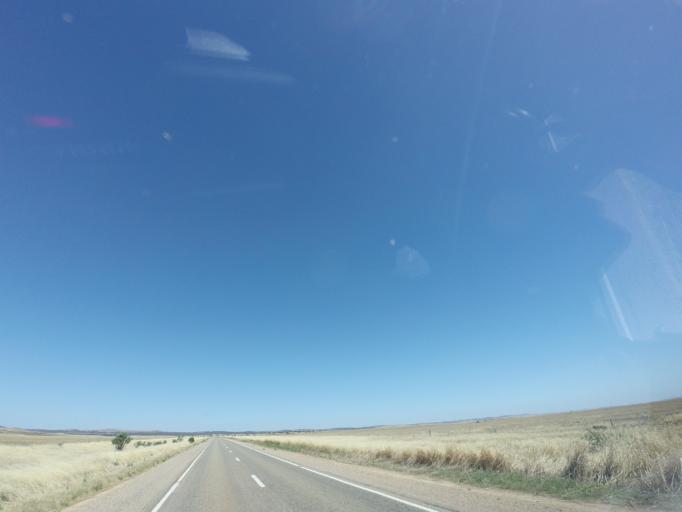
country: AU
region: South Australia
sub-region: Peterborough
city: Peterborough
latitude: -32.8325
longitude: 138.7113
